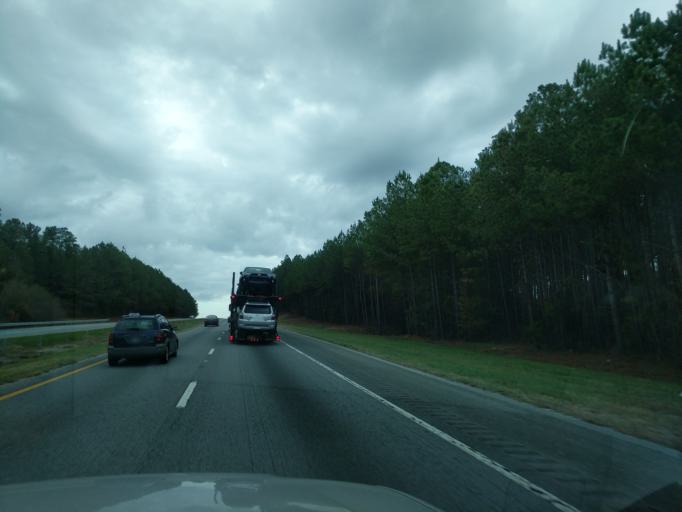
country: US
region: South Carolina
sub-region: Spartanburg County
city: Woodruff
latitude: 34.7708
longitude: -81.9536
